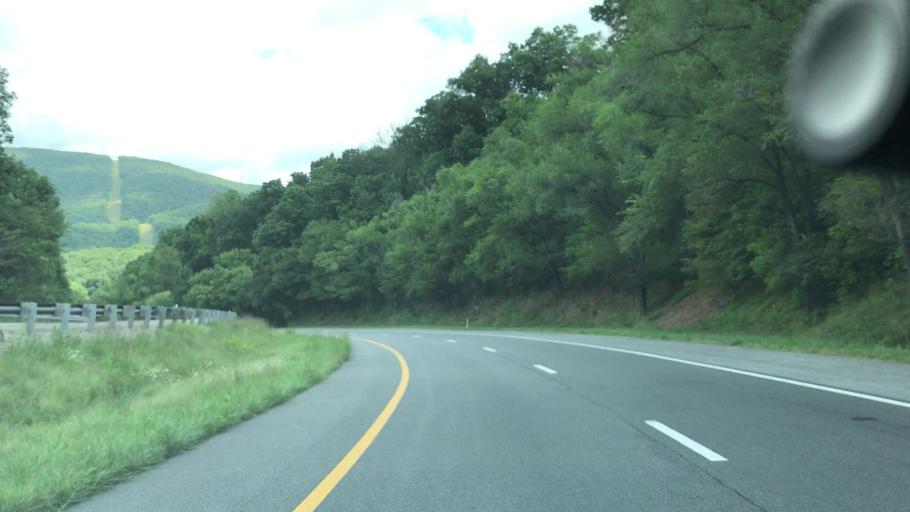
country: US
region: Virginia
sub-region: Giles County
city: Pearisburg
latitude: 37.3457
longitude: -80.7592
